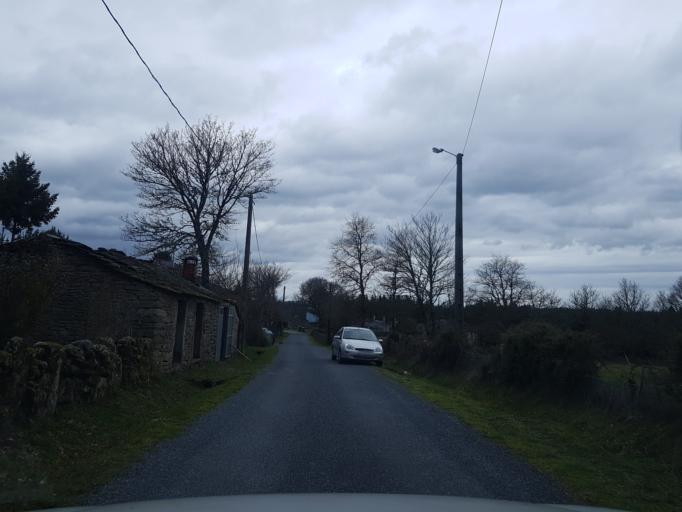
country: ES
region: Galicia
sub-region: Provincia de Lugo
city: Friol
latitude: 43.1191
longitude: -7.8157
